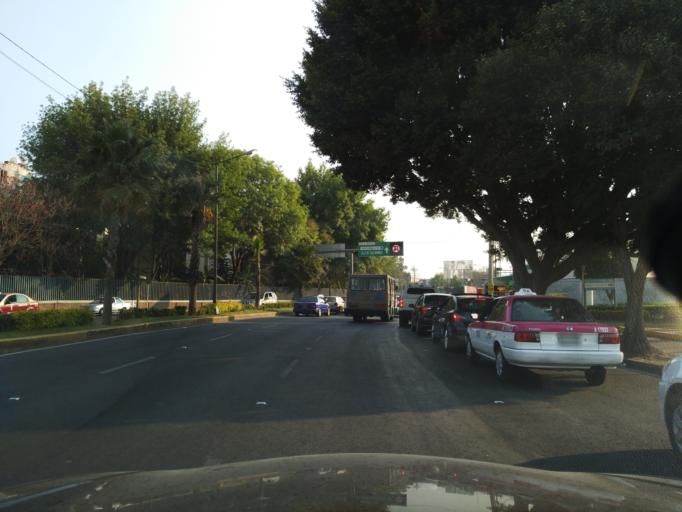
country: MX
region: Mexico City
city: Tlalpan
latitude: 19.3165
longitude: -99.1243
